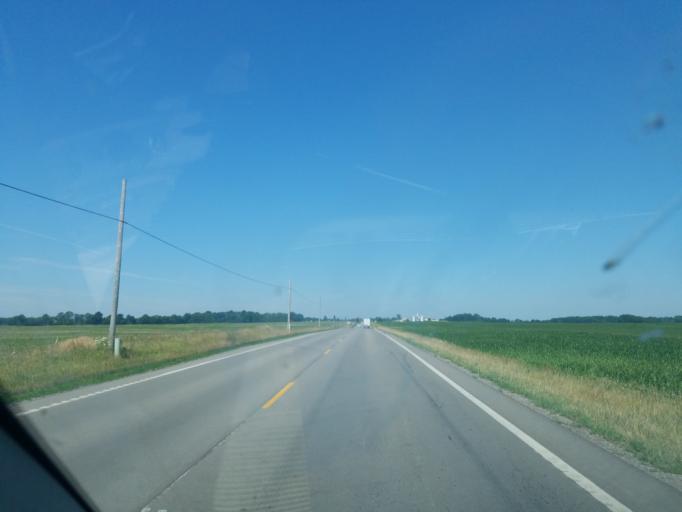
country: US
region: Ohio
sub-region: Shelby County
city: Jackson Center
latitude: 40.4393
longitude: -83.9979
